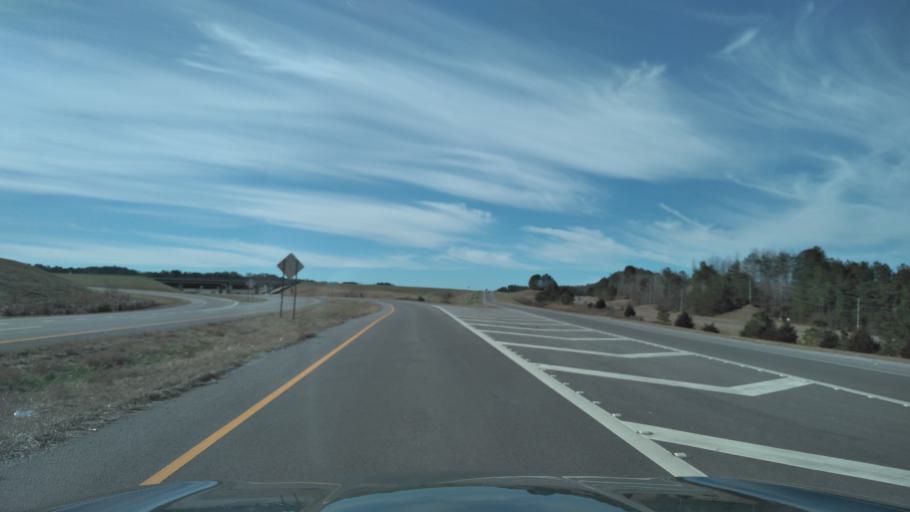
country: US
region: Alabama
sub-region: Walker County
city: Jasper
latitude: 33.8555
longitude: -87.3369
